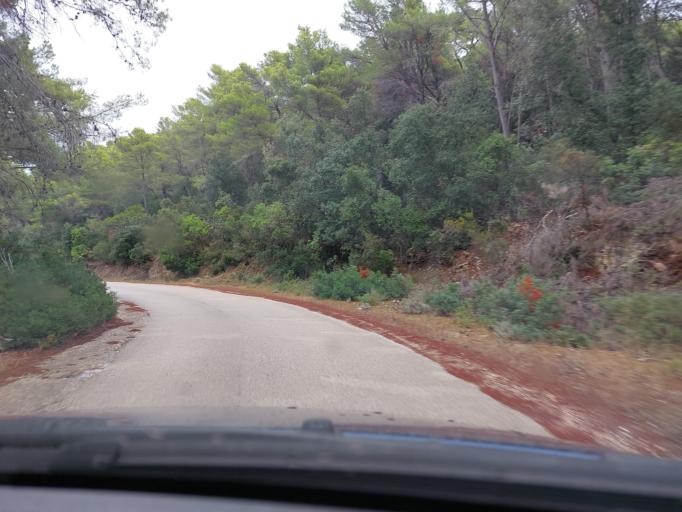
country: HR
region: Dubrovacko-Neretvanska
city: Smokvica
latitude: 42.7418
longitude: 16.8301
